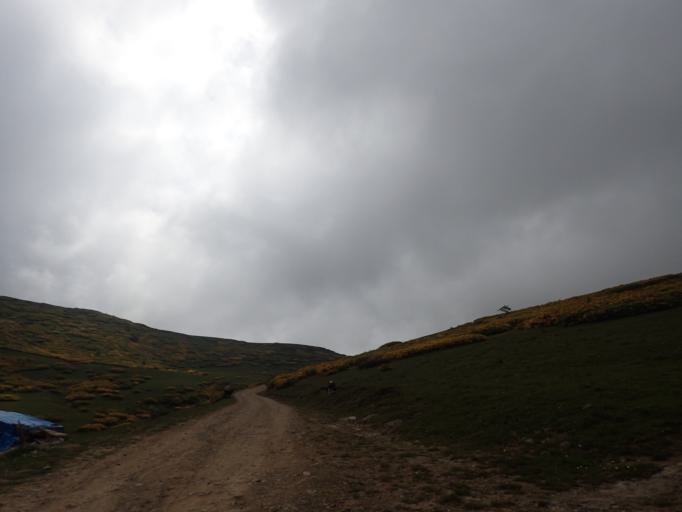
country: TR
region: Ordu
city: Topcam
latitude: 40.6365
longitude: 37.9282
